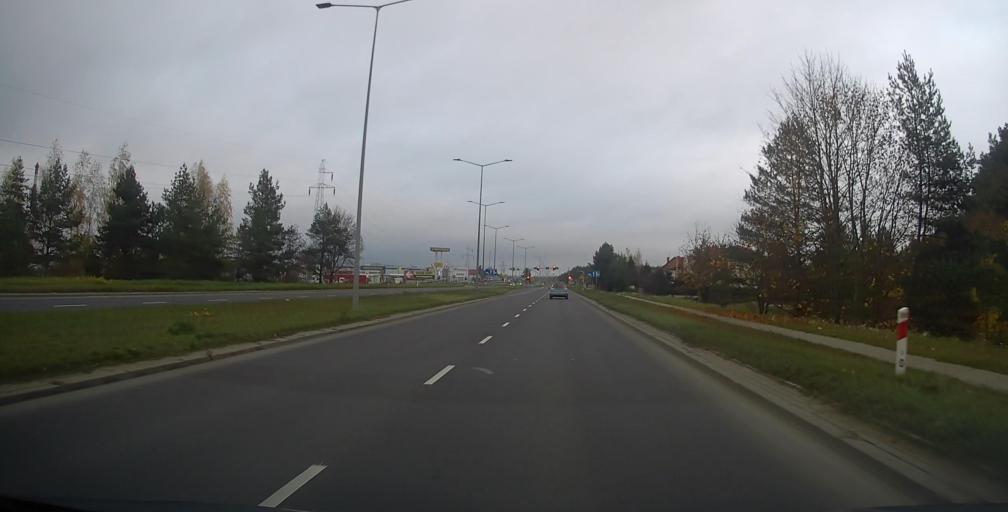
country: PL
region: Warmian-Masurian Voivodeship
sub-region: Powiat elcki
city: Elk
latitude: 53.8097
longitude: 22.3765
